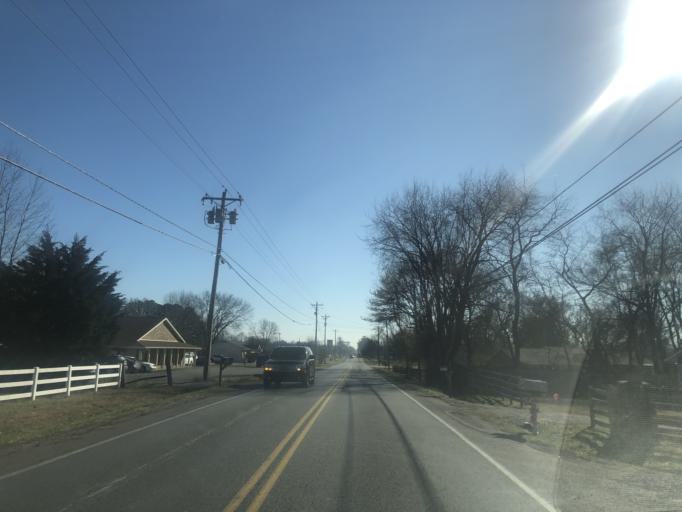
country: US
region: Tennessee
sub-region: Rutherford County
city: Smyrna
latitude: 35.9351
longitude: -86.4937
